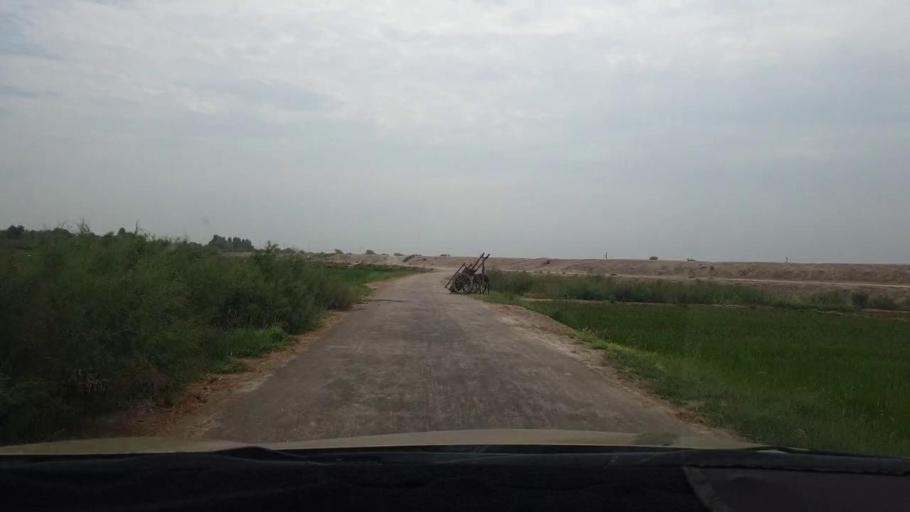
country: PK
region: Sindh
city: Naudero
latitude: 27.6213
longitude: 68.3321
